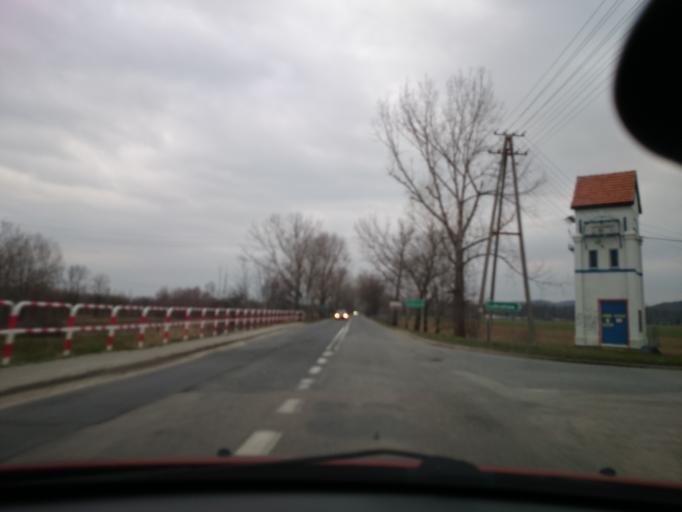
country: PL
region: Opole Voivodeship
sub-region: Powiat nyski
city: Paczkow
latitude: 50.4716
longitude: 17.0129
